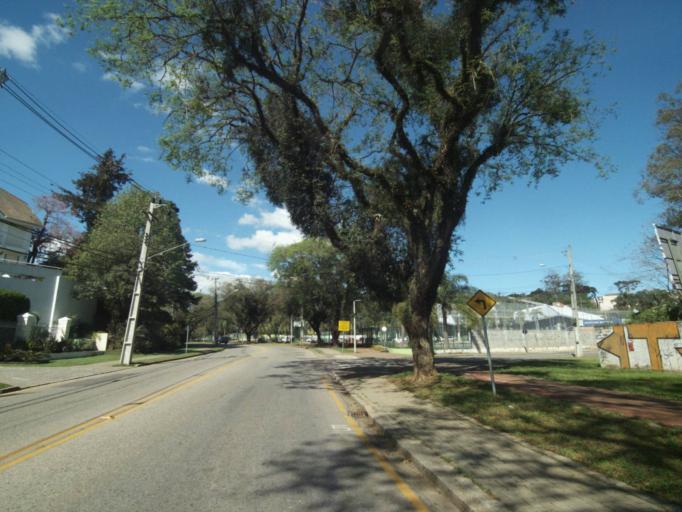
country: BR
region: Parana
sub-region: Curitiba
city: Curitiba
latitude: -25.3919
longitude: -49.2684
